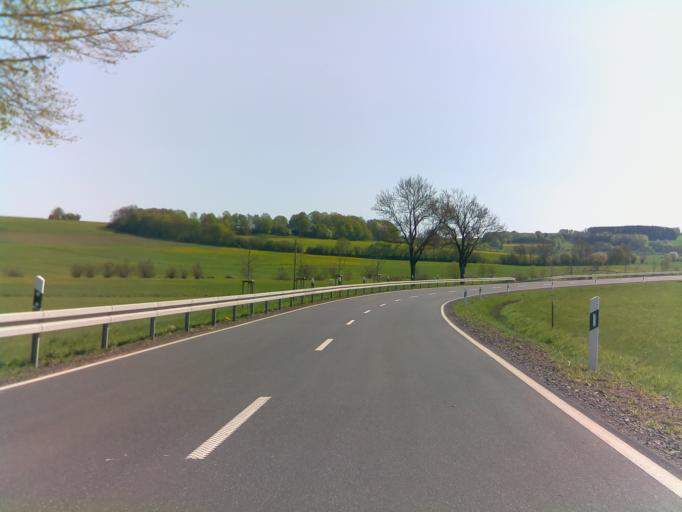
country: DE
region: Hesse
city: Herbstein
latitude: 50.5334
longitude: 9.3497
